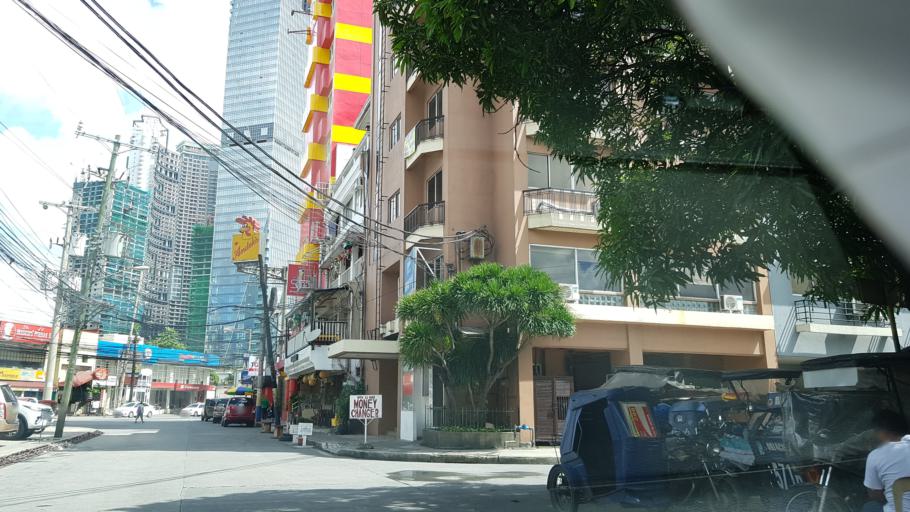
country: PH
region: Metro Manila
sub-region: Makati City
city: Makati City
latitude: 14.5622
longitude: 121.0287
